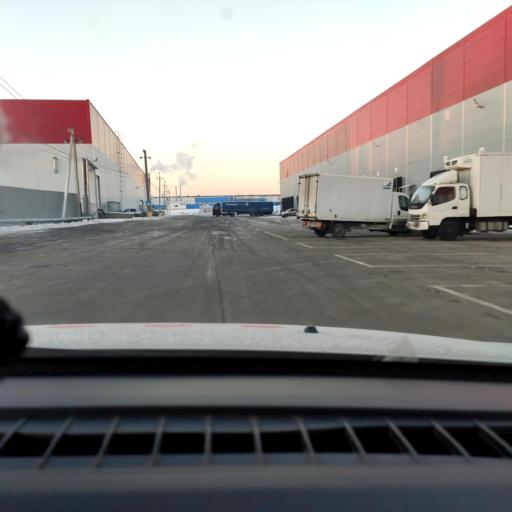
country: RU
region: Samara
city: Samara
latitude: 53.0999
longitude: 50.1370
